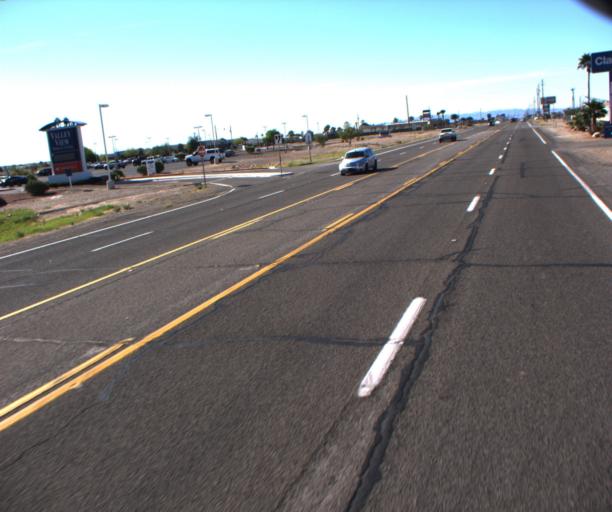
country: US
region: Arizona
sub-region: Mohave County
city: Mohave Valley
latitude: 35.0027
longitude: -114.5981
